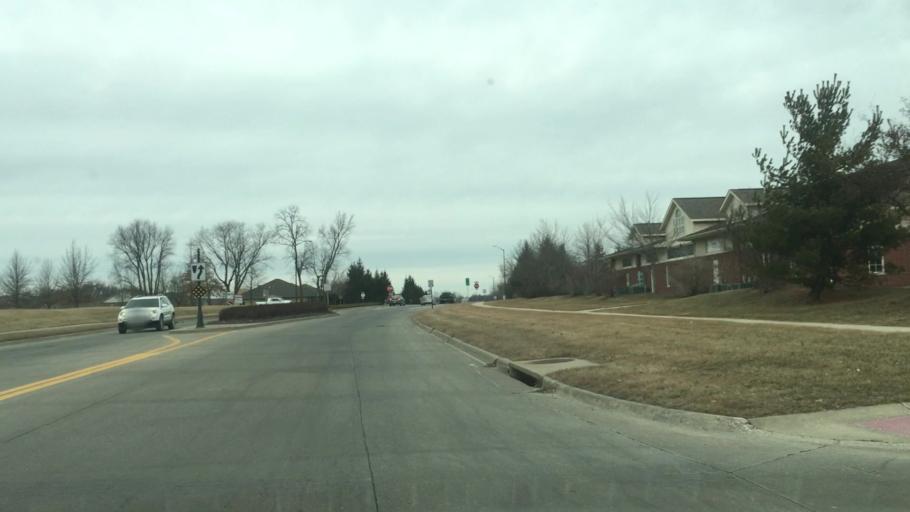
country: US
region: Iowa
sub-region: Johnson County
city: Coralville
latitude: 41.7030
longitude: -91.5877
